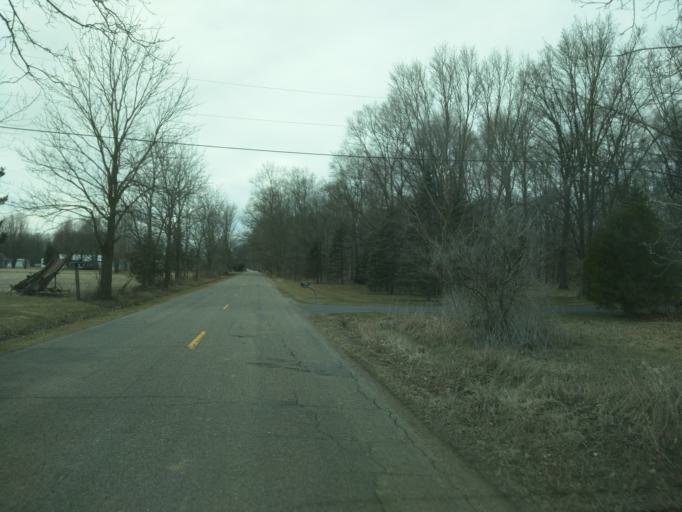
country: US
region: Michigan
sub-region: Ingham County
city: Okemos
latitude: 42.6690
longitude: -84.3765
